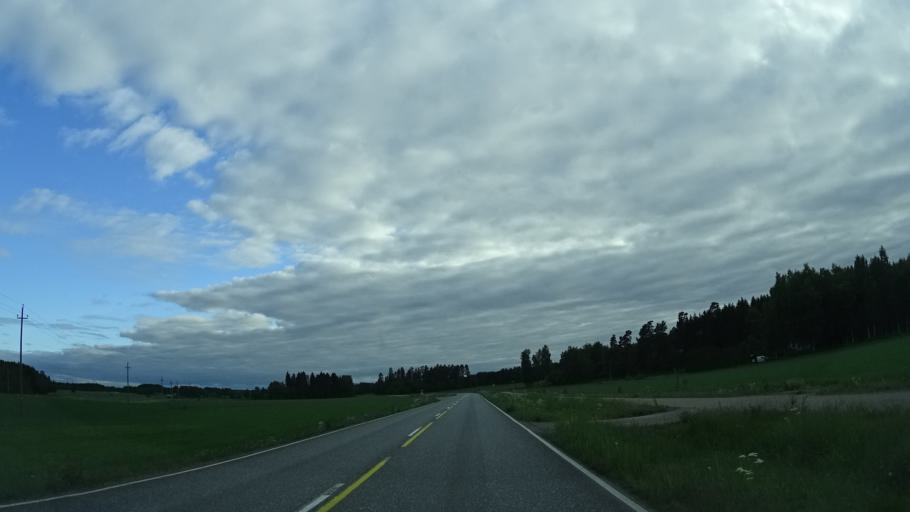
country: FI
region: Paijanne Tavastia
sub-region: Lahti
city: Asikkala
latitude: 61.2515
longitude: 25.5075
